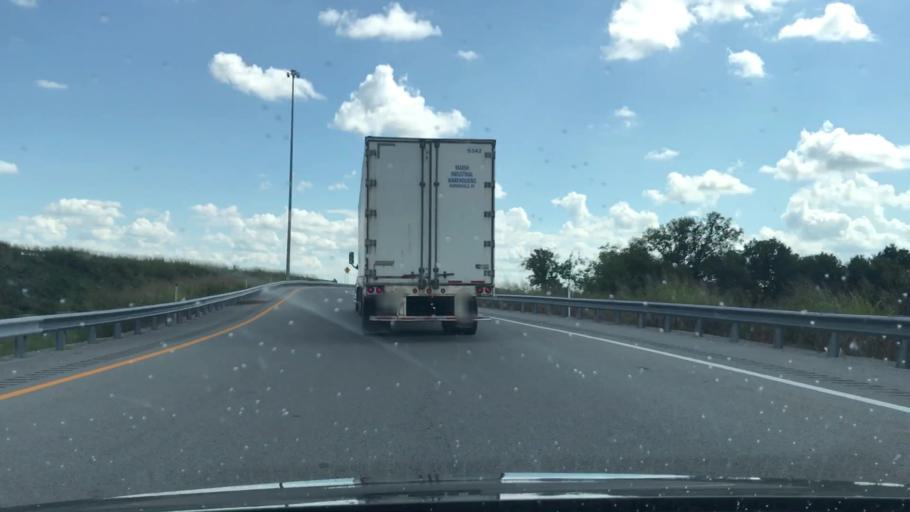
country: US
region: Kentucky
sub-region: Christian County
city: Hopkinsville
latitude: 36.8173
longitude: -87.4848
